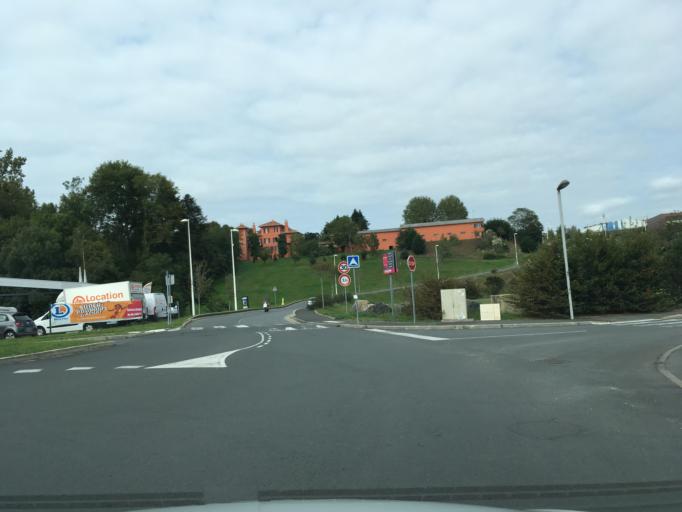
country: FR
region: Aquitaine
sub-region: Departement des Pyrenees-Atlantiques
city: Biarritz
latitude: 43.4630
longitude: -1.5386
